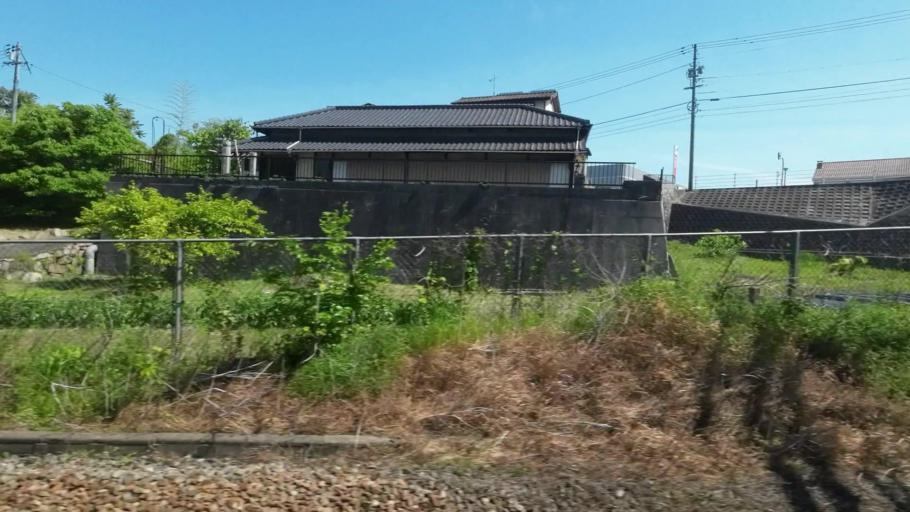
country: JP
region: Hiroshima
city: Fukuyama
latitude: 34.4743
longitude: 133.3099
